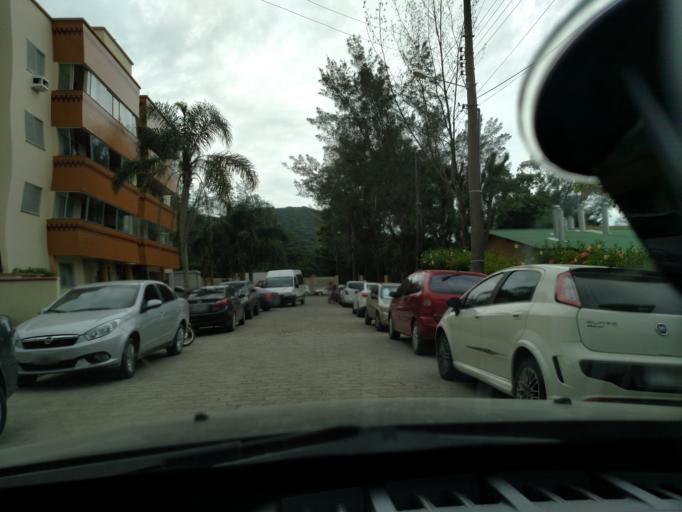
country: BR
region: Santa Catarina
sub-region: Porto Belo
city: Porto Belo
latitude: -27.1703
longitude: -48.4997
